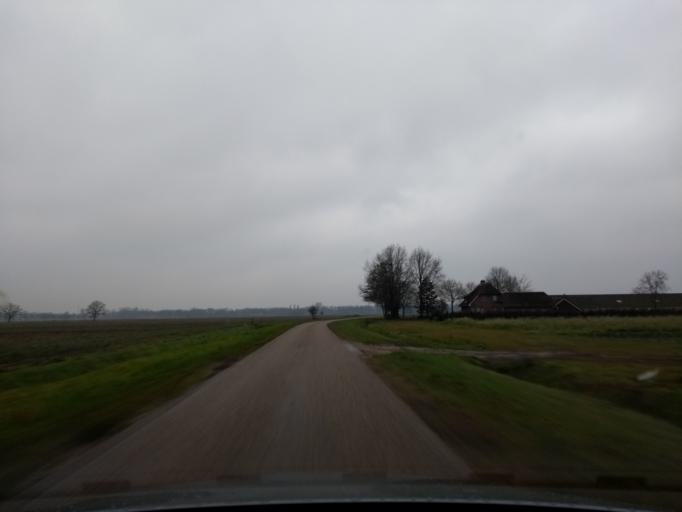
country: NL
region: Overijssel
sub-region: Gemeente Twenterand
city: Vriezenveen
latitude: 52.4085
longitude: 6.6572
